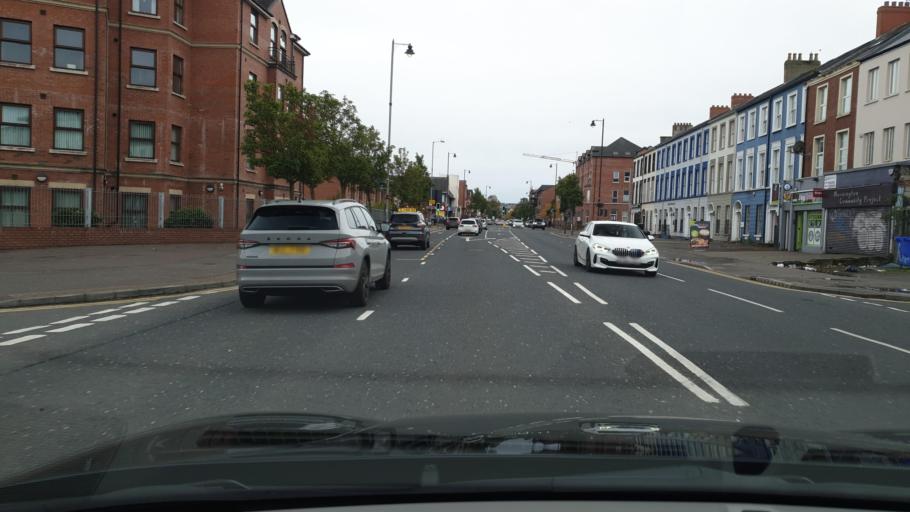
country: GB
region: Northern Ireland
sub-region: City of Belfast
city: Belfast
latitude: 54.5875
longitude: -5.9238
